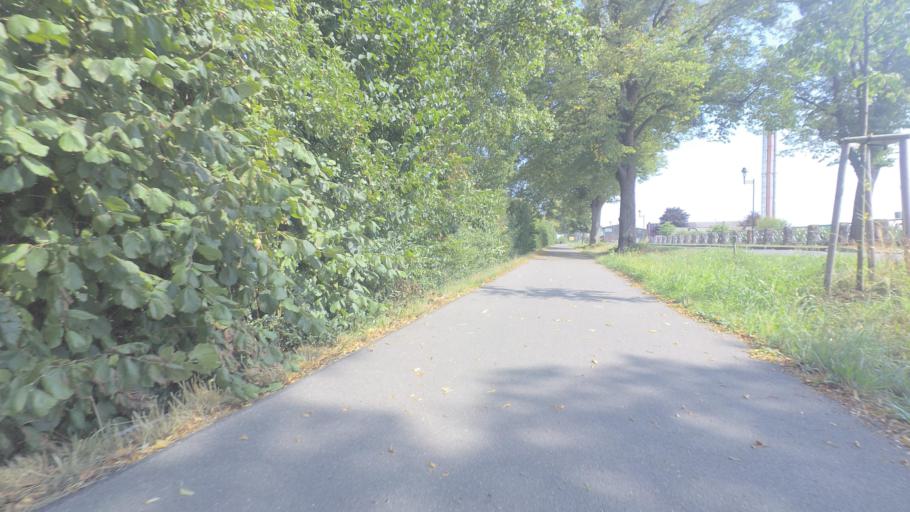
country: DE
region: Mecklenburg-Vorpommern
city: Malchin
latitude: 53.7344
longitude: 12.7499
